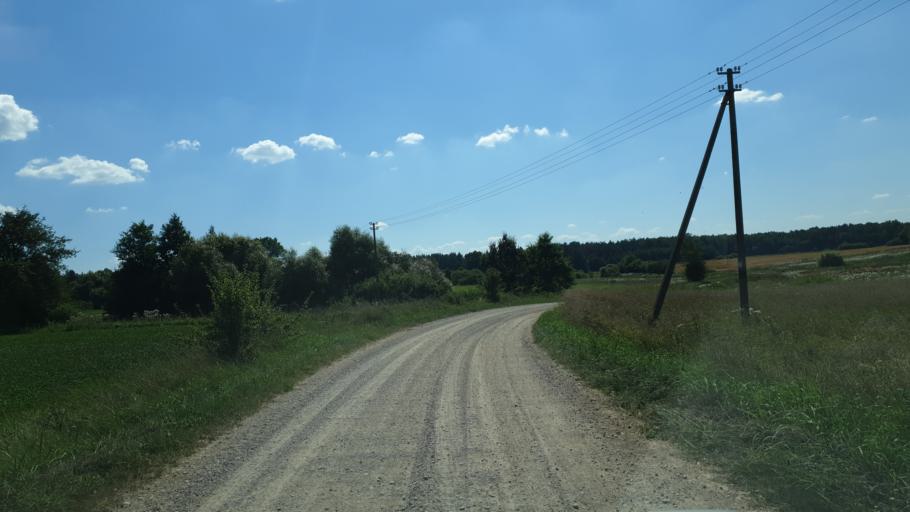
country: LT
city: Sirvintos
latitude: 54.9046
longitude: 24.9108
